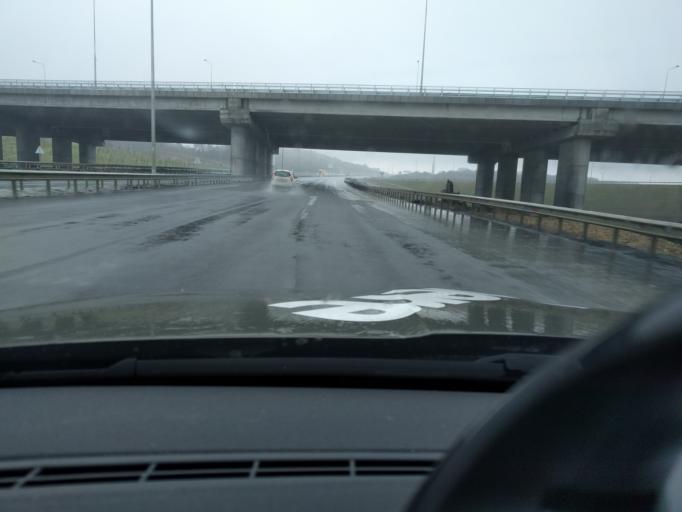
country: TR
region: Istanbul
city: Durusu
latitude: 41.2587
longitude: 28.6816
